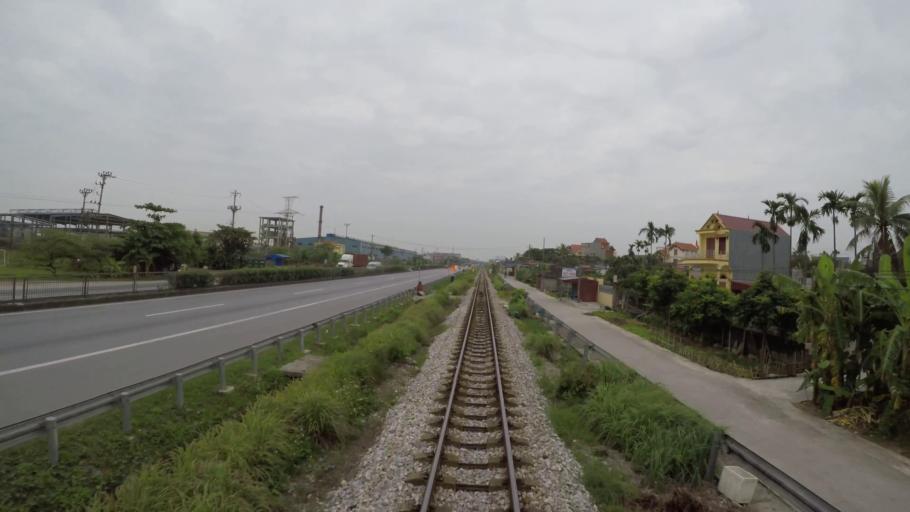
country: VN
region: Hai Duong
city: Phu Thai
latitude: 20.9471
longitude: 106.5377
